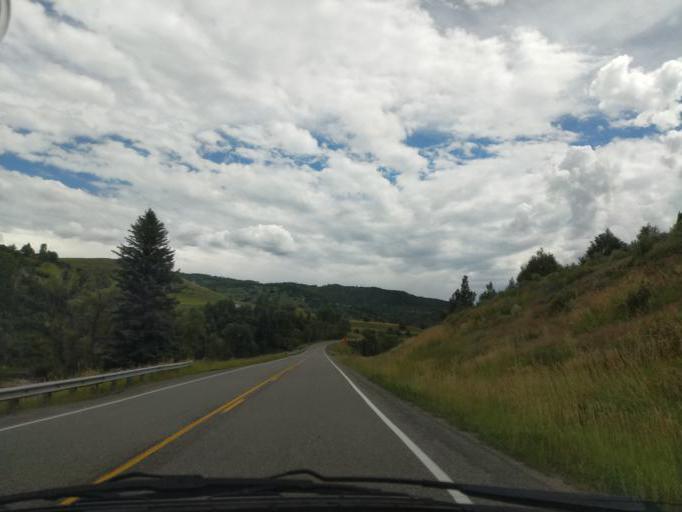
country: US
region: Colorado
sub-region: Delta County
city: Paonia
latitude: 39.0553
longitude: -107.3631
